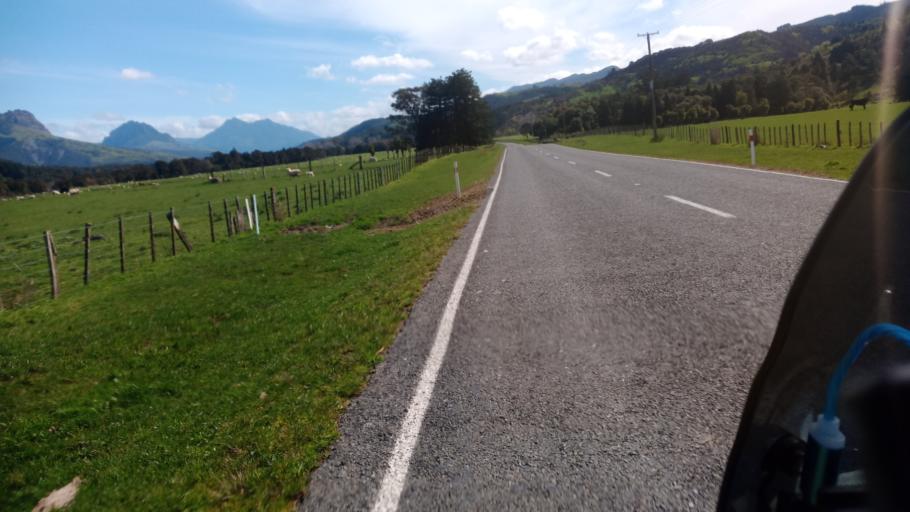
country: NZ
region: Gisborne
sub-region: Gisborne District
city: Gisborne
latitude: -37.8679
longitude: 178.2651
